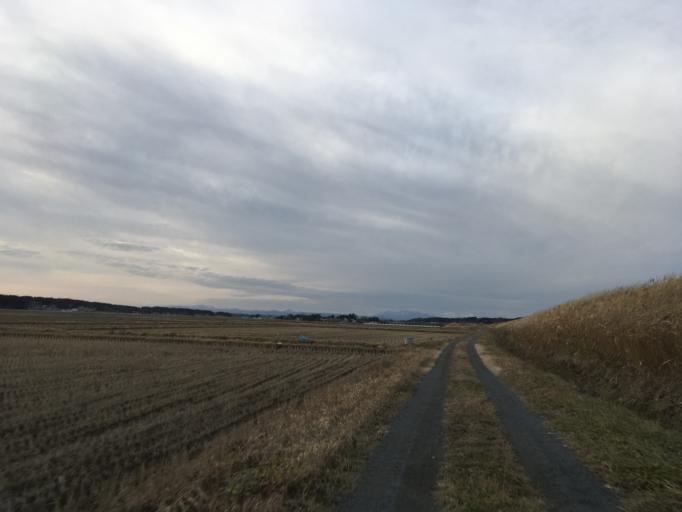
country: JP
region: Miyagi
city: Kogota
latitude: 38.6465
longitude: 141.0689
